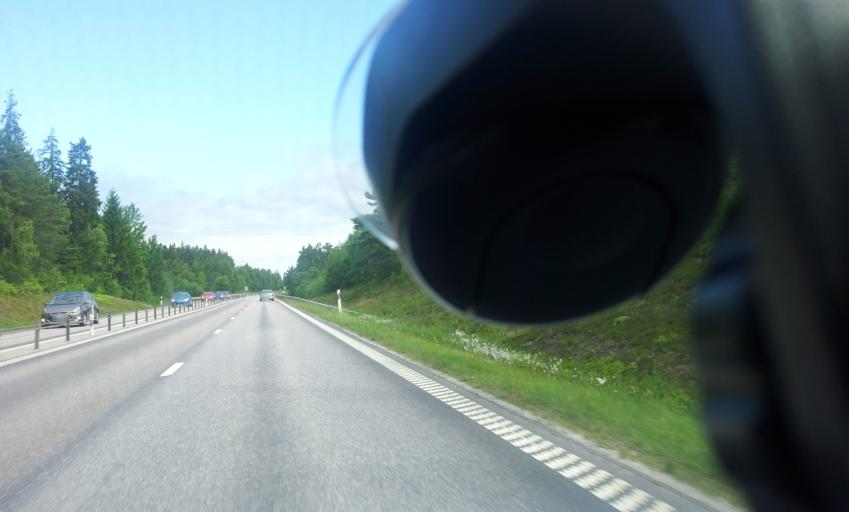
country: SE
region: Kalmar
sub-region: Kalmar Kommun
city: Lindsdal
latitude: 56.7357
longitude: 16.3100
